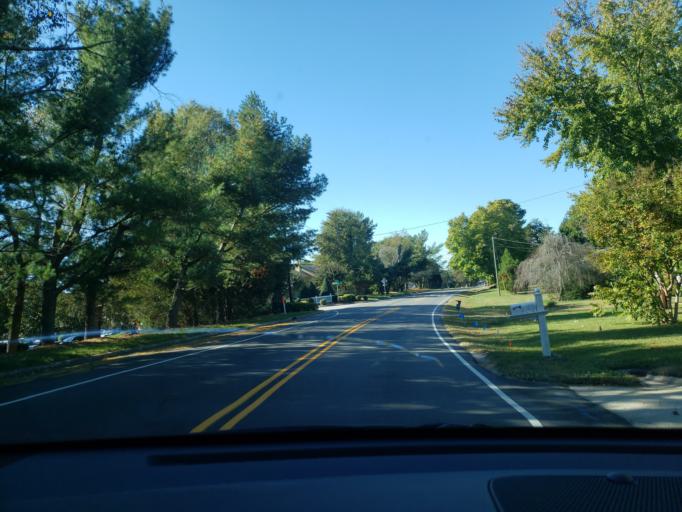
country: US
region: North Carolina
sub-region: Wake County
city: Raleigh
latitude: 35.8188
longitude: -78.5764
